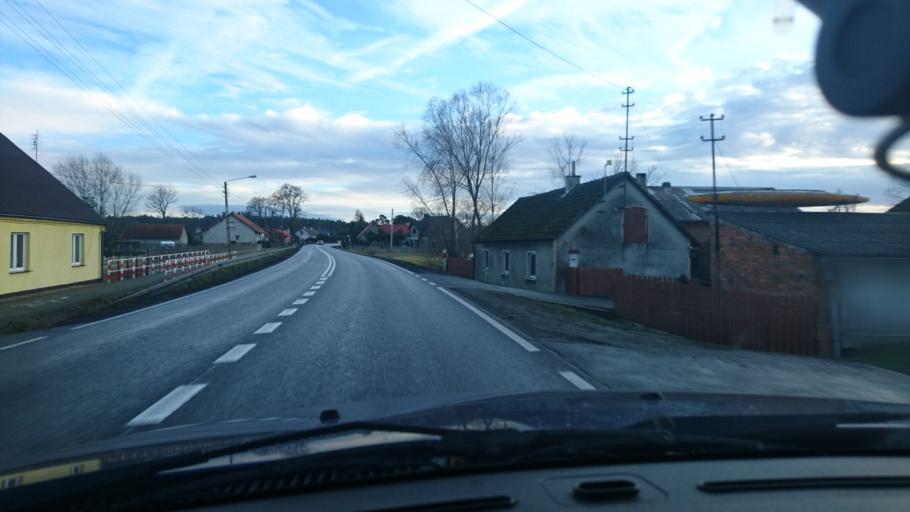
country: PL
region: Greater Poland Voivodeship
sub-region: Powiat ostrzeszowski
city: Ostrzeszow
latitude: 51.3507
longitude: 17.9479
